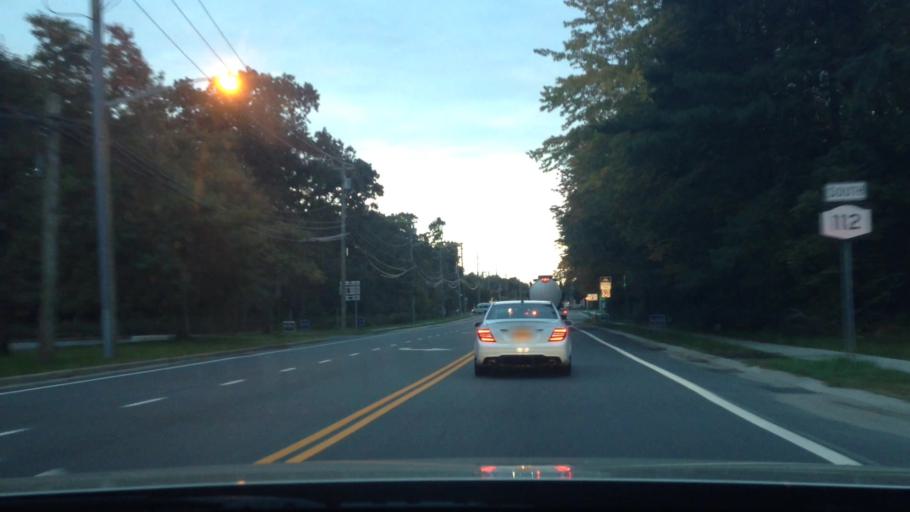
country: US
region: New York
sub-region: Suffolk County
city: Coram
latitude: 40.8675
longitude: -72.9995
